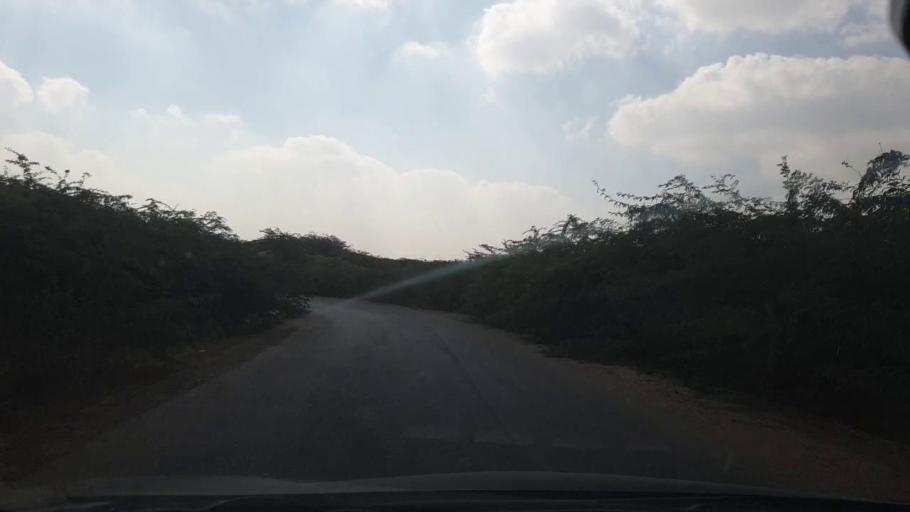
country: PK
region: Sindh
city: Malir Cantonment
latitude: 25.0148
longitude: 67.3526
